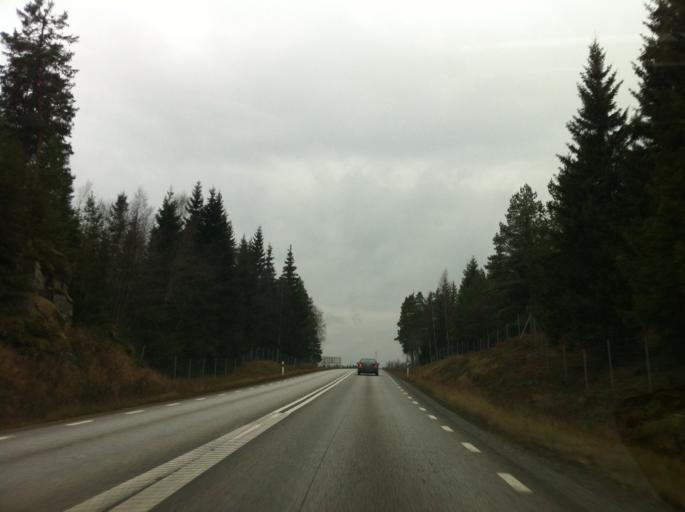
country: SE
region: Joenkoeping
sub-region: Savsjo Kommun
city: Saevsjoe
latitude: 57.3959
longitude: 14.6540
